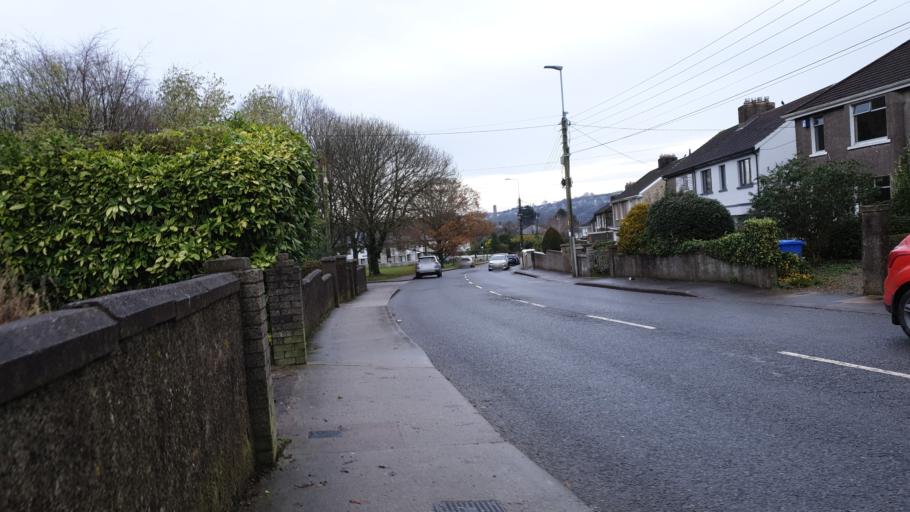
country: IE
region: Munster
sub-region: County Cork
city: Cork
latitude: 51.8916
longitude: -8.4278
